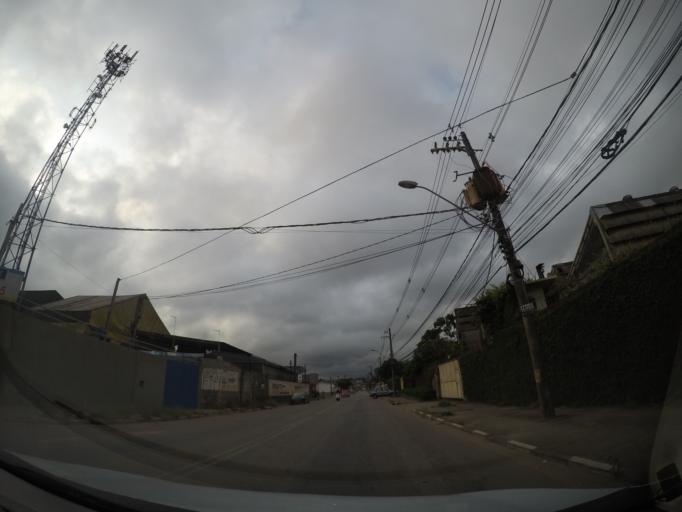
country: BR
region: Sao Paulo
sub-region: Aruja
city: Aruja
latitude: -23.4176
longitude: -46.3828
